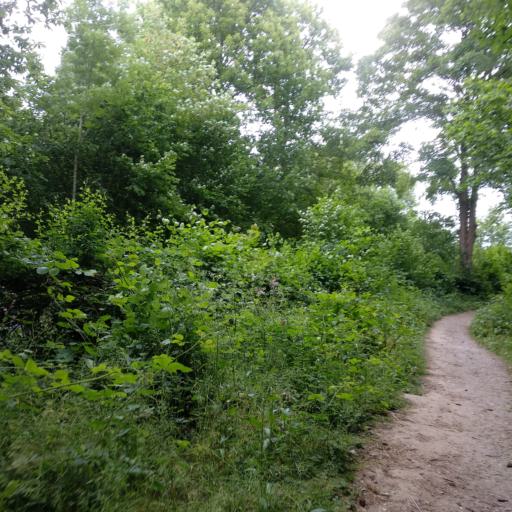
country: GB
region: England
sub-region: Kent
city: Ashford
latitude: 51.1642
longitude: 0.8335
